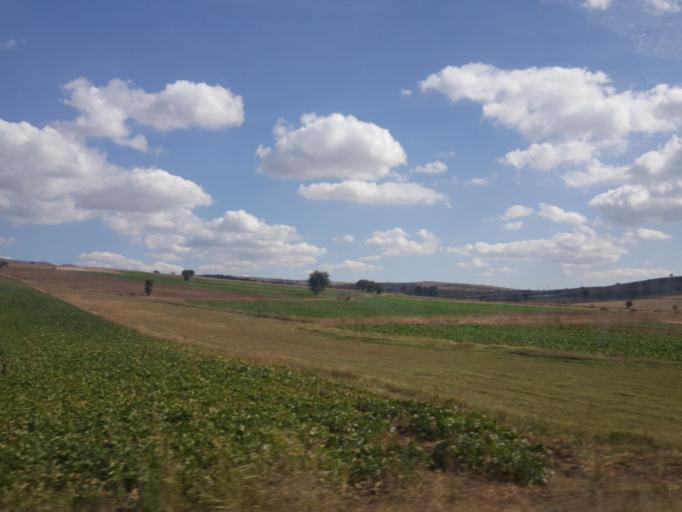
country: TR
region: Tokat
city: Camlibel
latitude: 40.1967
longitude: 36.4648
